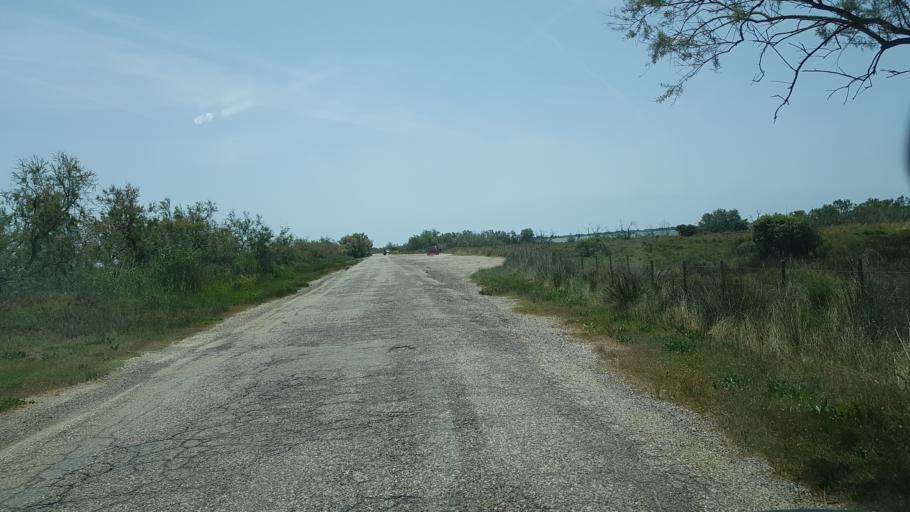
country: FR
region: Provence-Alpes-Cote d'Azur
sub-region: Departement des Bouches-du-Rhone
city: Arles
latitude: 43.5470
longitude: 4.6298
